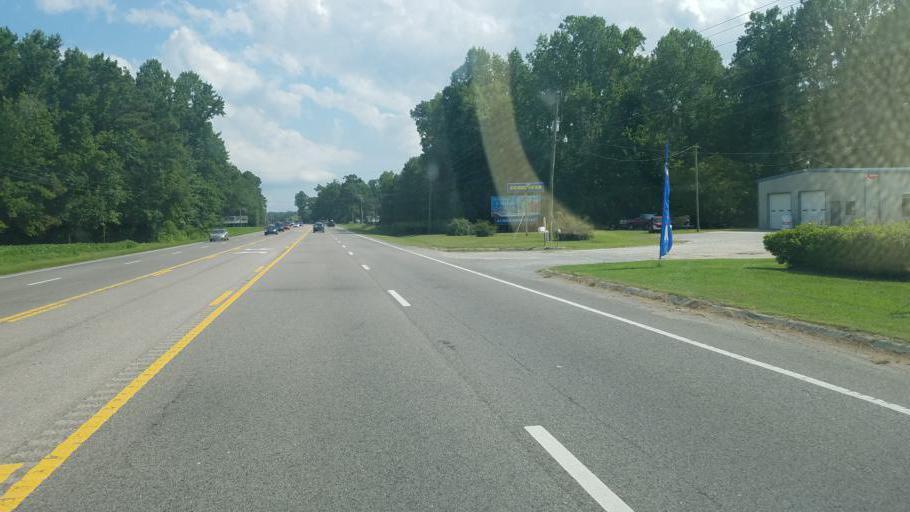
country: US
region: North Carolina
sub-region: Currituck County
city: Currituck
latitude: 36.2907
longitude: -75.9214
